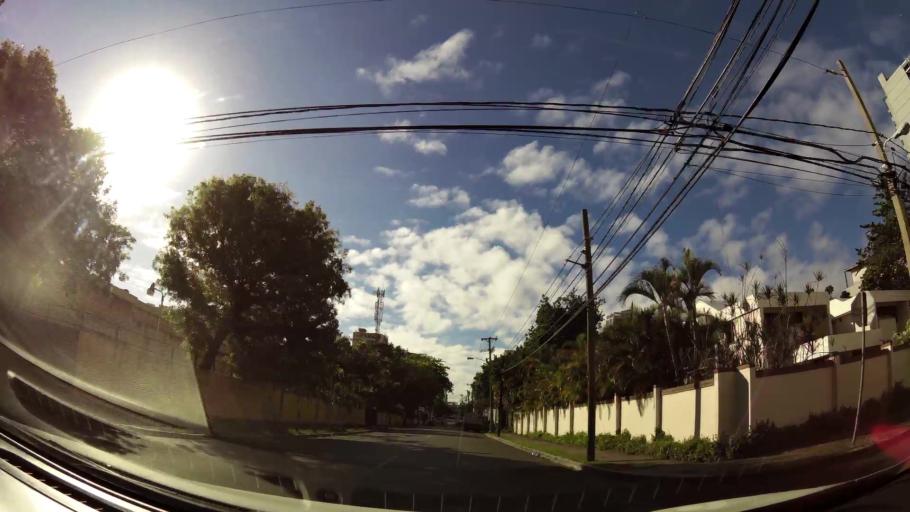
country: DO
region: Nacional
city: La Julia
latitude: 18.4738
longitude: -69.9399
